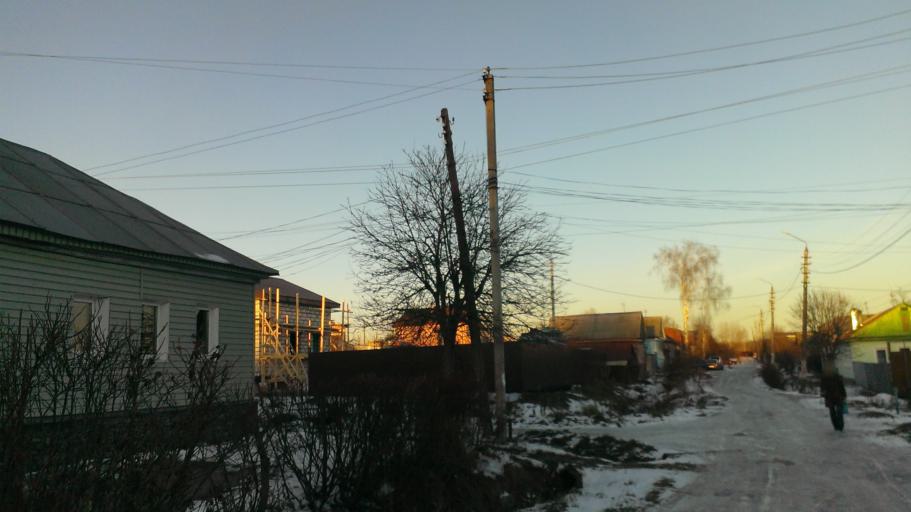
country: RU
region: Tula
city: Tula
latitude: 54.1979
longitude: 37.6953
